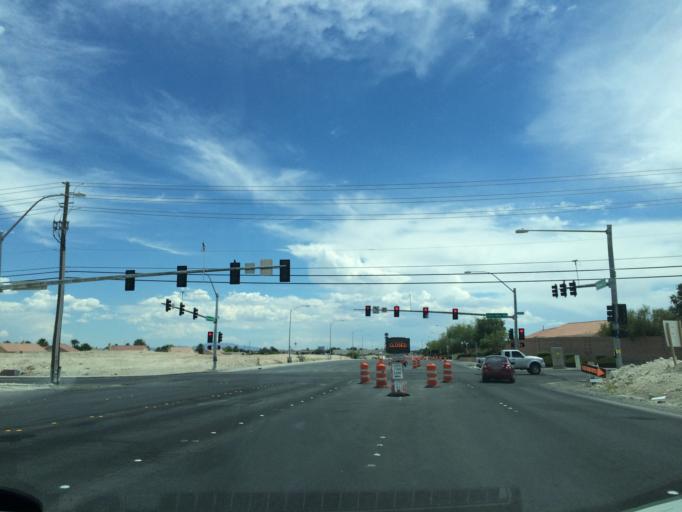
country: US
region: Nevada
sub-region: Clark County
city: North Las Vegas
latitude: 36.2474
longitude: -115.1802
